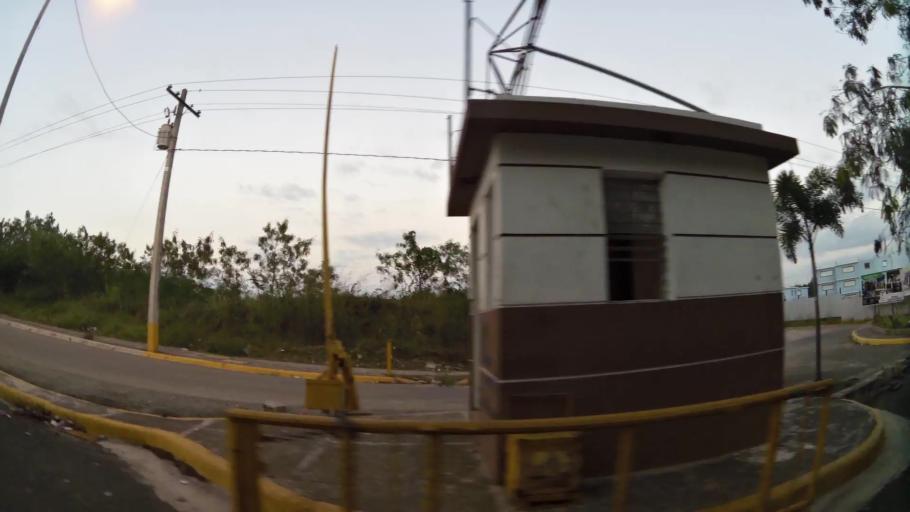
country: DO
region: Nacional
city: La Agustina
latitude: 18.5429
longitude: -69.9497
